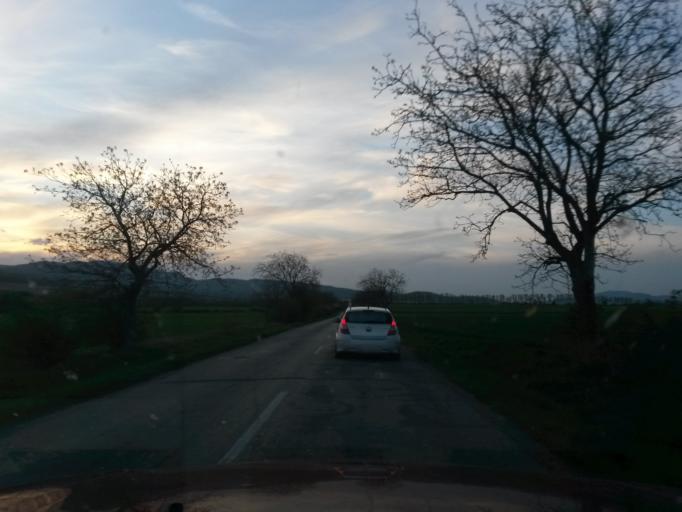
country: HU
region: Borsod-Abauj-Zemplen
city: Satoraljaujhely
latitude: 48.5332
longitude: 21.5773
